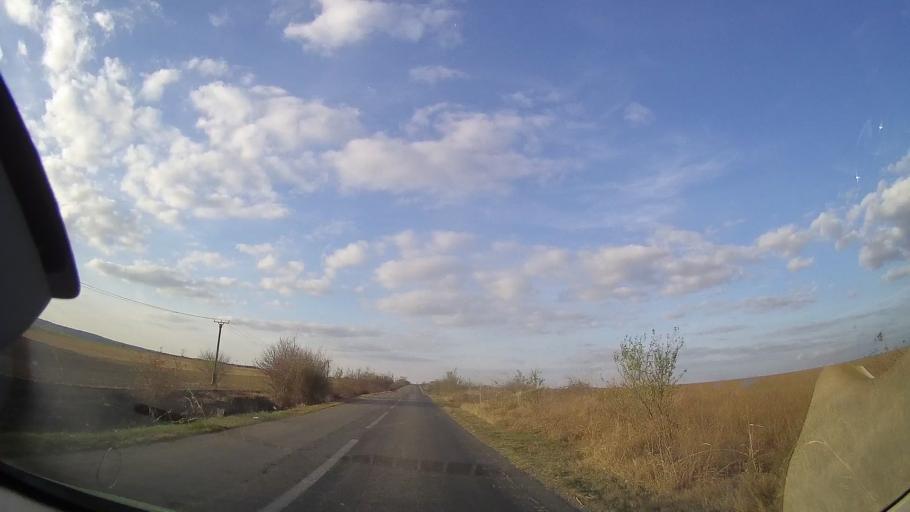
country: RO
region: Constanta
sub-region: Comuna Dumbraveni
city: Dumbraveni
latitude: 43.9300
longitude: 28.0282
